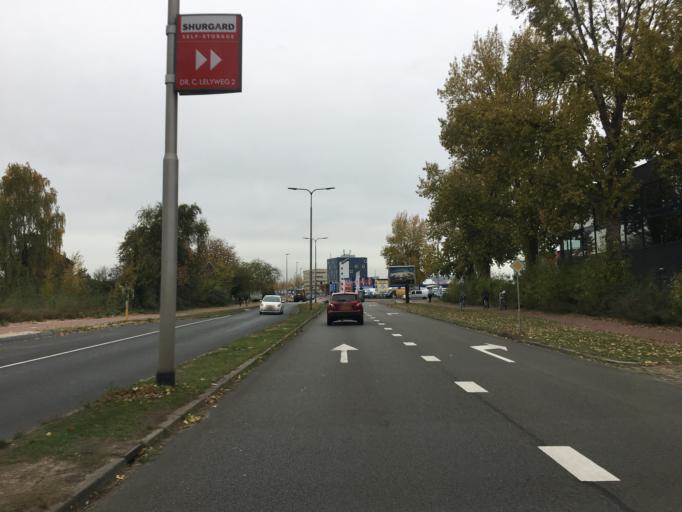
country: NL
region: Gelderland
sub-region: Gemeente Arnhem
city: Arnhem
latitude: 51.9714
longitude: 5.9370
